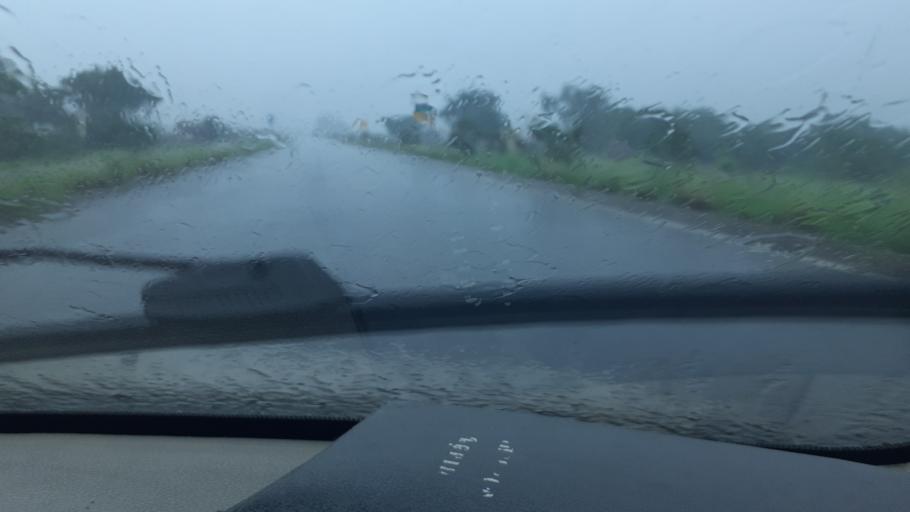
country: IN
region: Tamil Nadu
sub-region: Virudhunagar
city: Sattur
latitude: 9.4436
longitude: 77.9258
